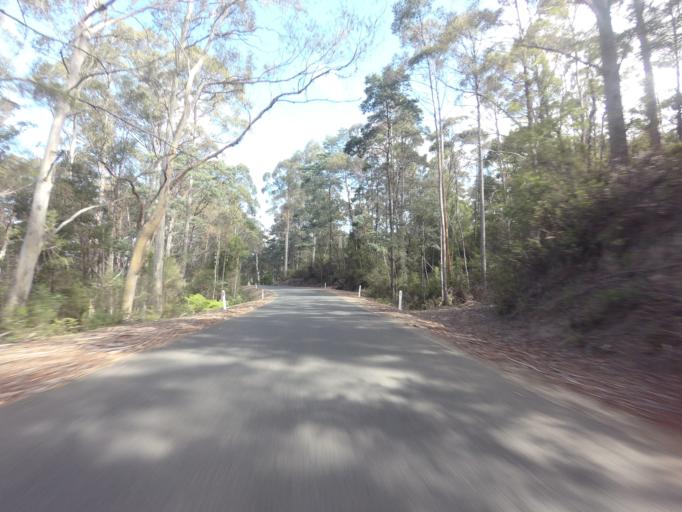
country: AU
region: Tasmania
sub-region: Break O'Day
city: St Helens
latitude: -41.6546
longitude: 148.2461
